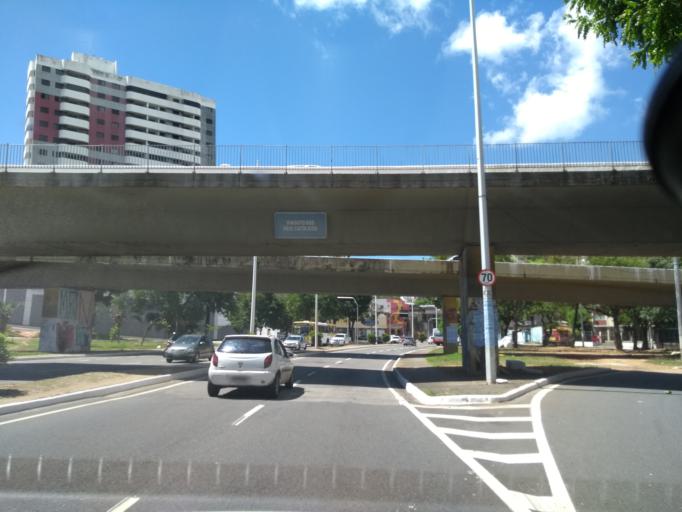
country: BR
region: Bahia
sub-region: Salvador
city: Salvador
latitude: -12.9953
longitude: -38.5153
